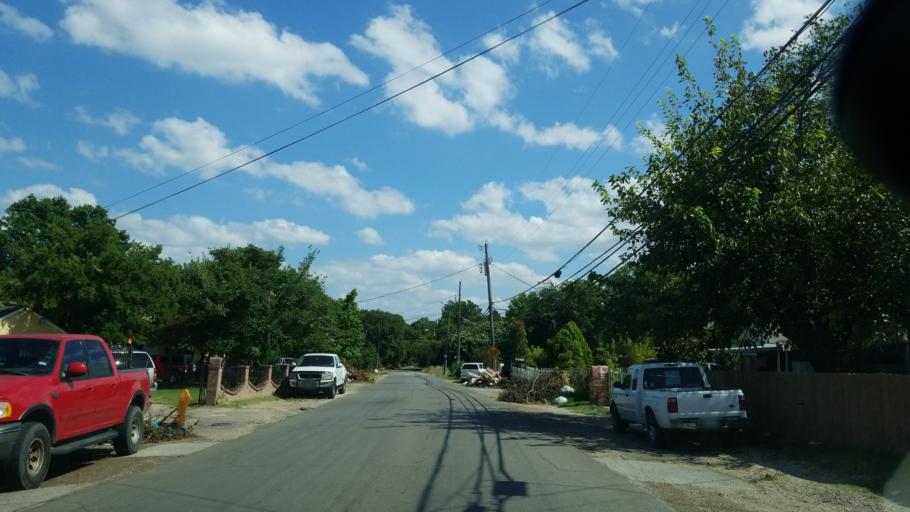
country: US
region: Texas
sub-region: Dallas County
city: Balch Springs
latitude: 32.7711
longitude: -96.6964
